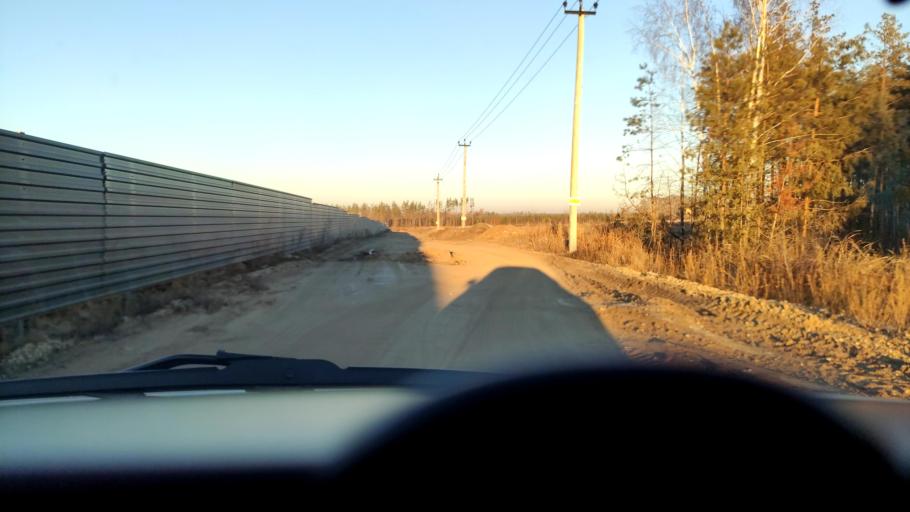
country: RU
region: Voronezj
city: Podgornoye
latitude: 51.7500
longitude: 39.1414
